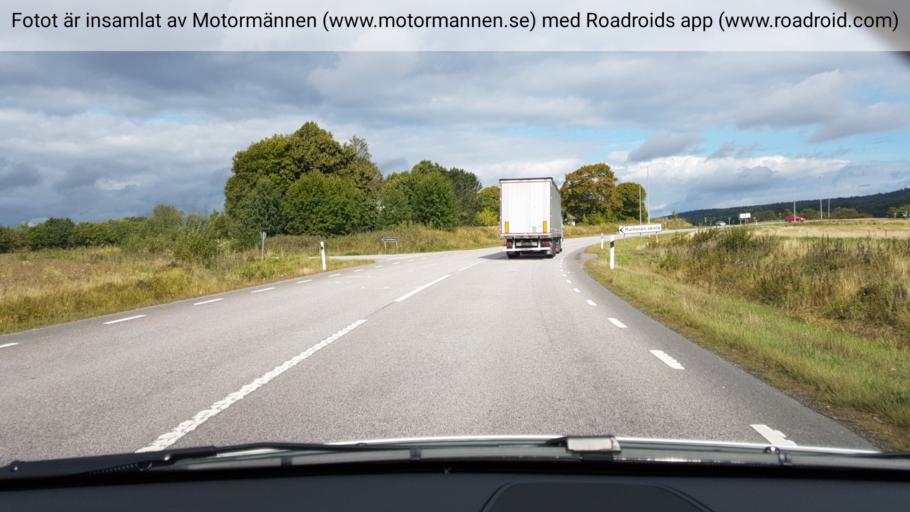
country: SE
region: Vaestra Goetaland
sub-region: Vanersborgs Kommun
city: Vargon
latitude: 58.2883
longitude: 12.3939
